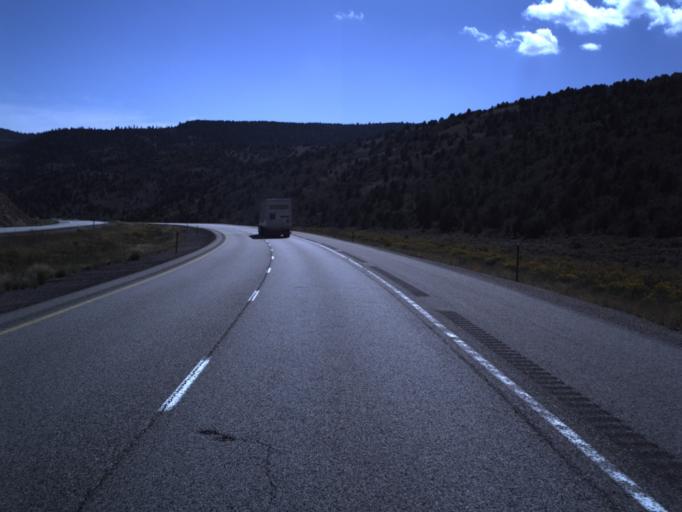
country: US
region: Utah
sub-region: Wayne County
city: Loa
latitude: 38.7683
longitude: -111.4716
